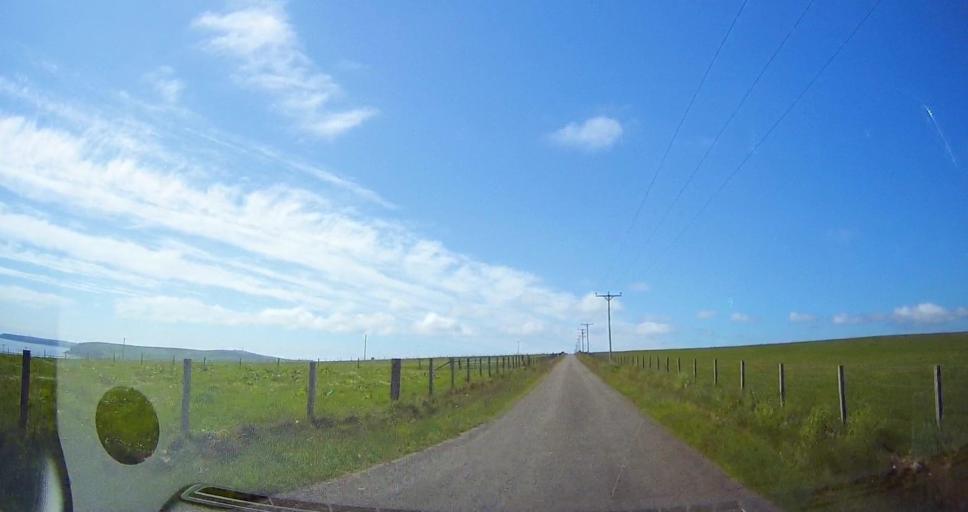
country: GB
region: Scotland
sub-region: Orkney Islands
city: Kirkwall
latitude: 58.8168
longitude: -2.9129
